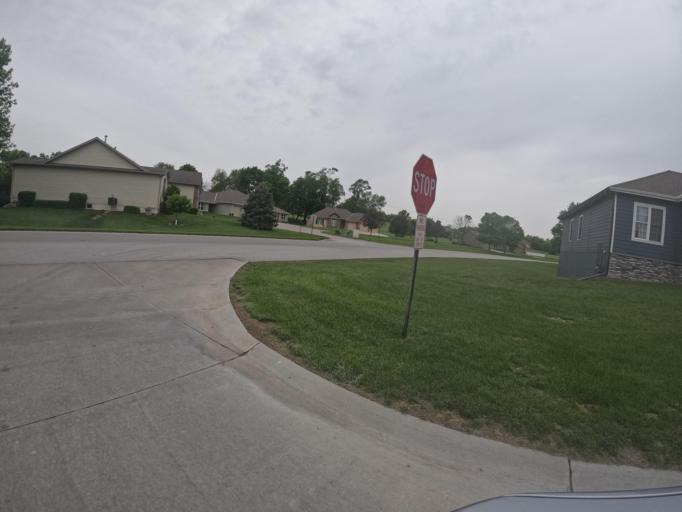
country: US
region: Nebraska
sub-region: Sarpy County
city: Offutt Air Force Base
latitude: 41.0476
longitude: -95.9550
